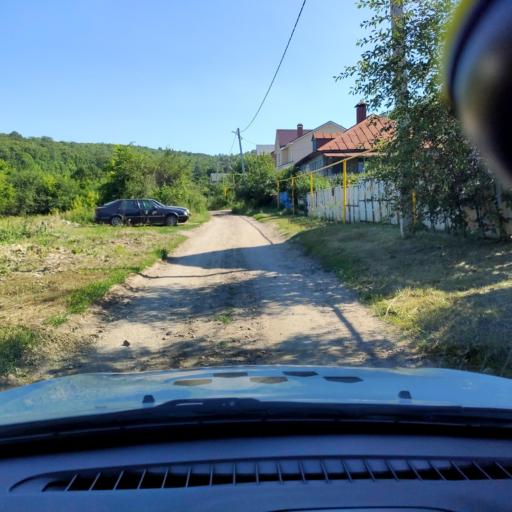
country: RU
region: Samara
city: Zhigulevsk
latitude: 53.3952
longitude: 49.5295
